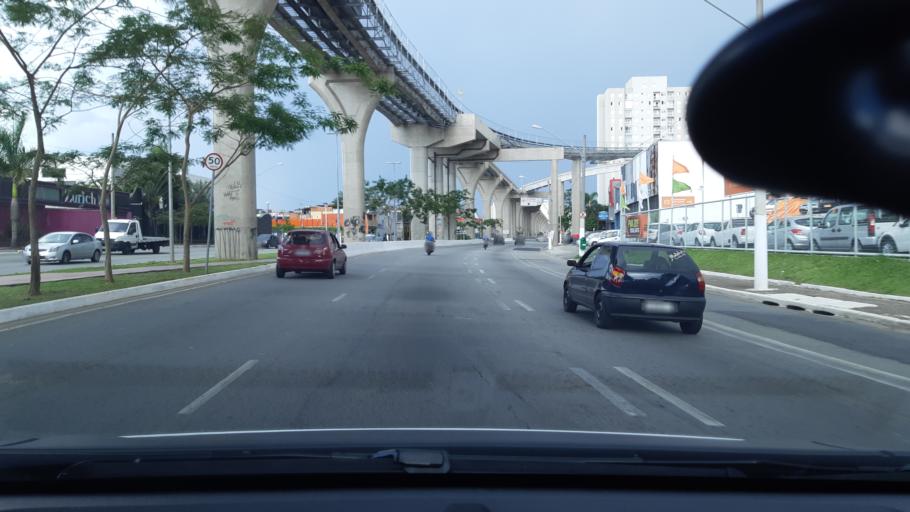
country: BR
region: Sao Paulo
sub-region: Sao Caetano Do Sul
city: Sao Caetano do Sul
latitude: -23.5818
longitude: -46.5595
